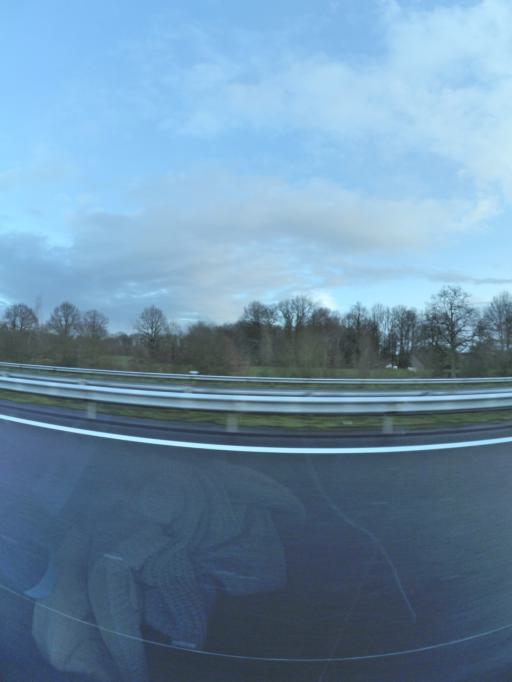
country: FR
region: Pays de la Loire
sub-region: Departement de la Sarthe
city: Parce-sur-Sarthe
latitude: 47.7963
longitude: -0.1754
